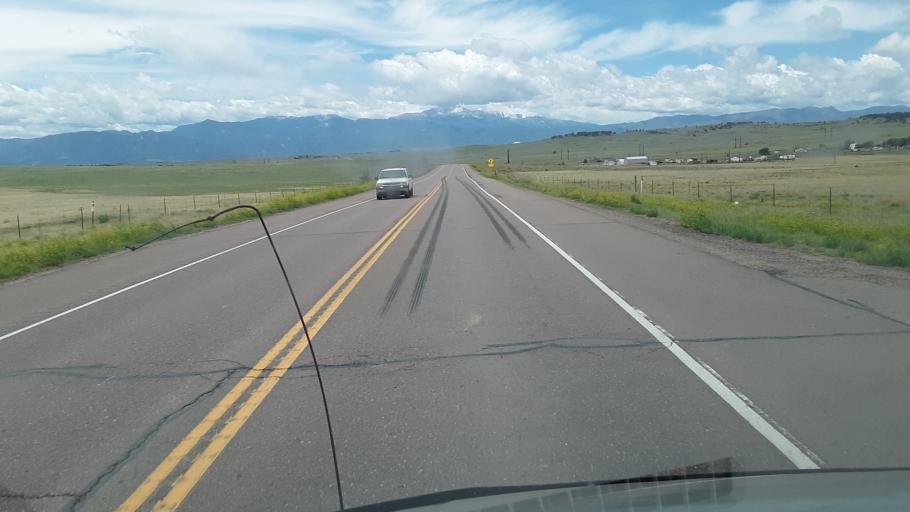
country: US
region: Colorado
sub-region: El Paso County
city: Cimarron Hills
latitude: 38.8387
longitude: -104.6056
